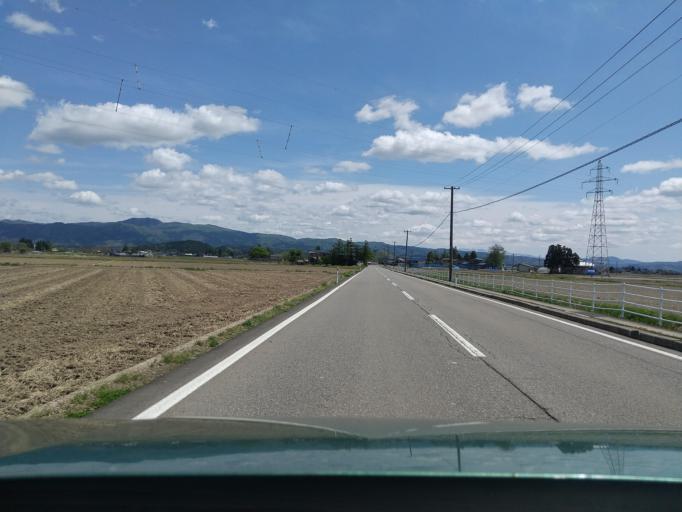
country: JP
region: Akita
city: Omagari
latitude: 39.3858
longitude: 140.5128
